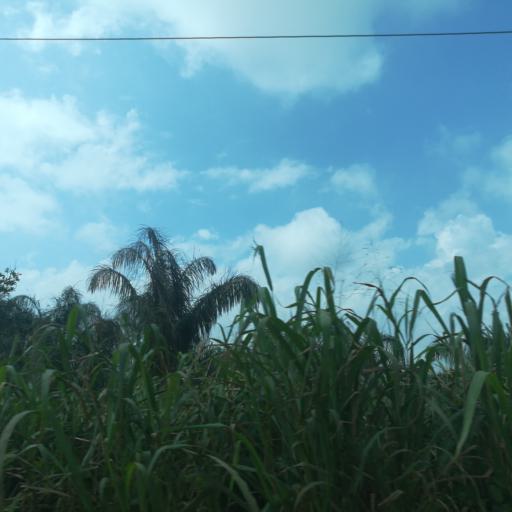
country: NG
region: Lagos
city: Ikorodu
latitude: 6.6716
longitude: 3.6652
